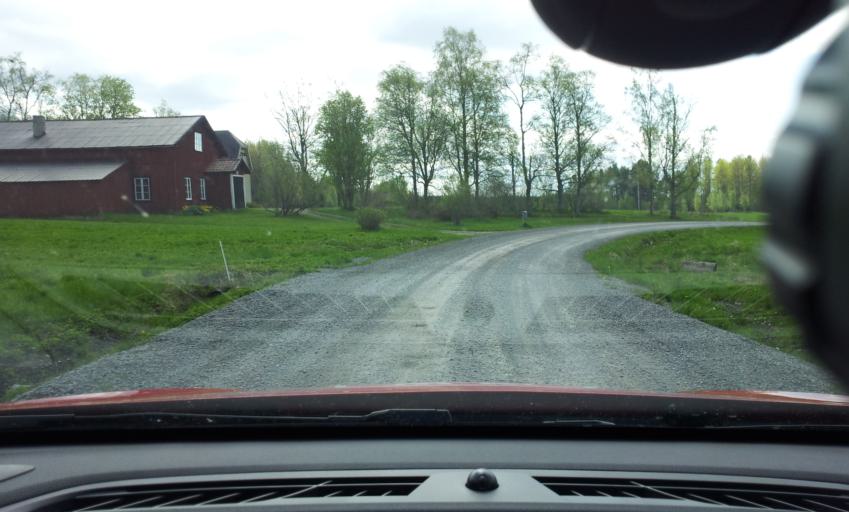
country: SE
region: Jaemtland
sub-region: OEstersunds Kommun
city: Ostersund
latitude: 63.0501
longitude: 14.5704
